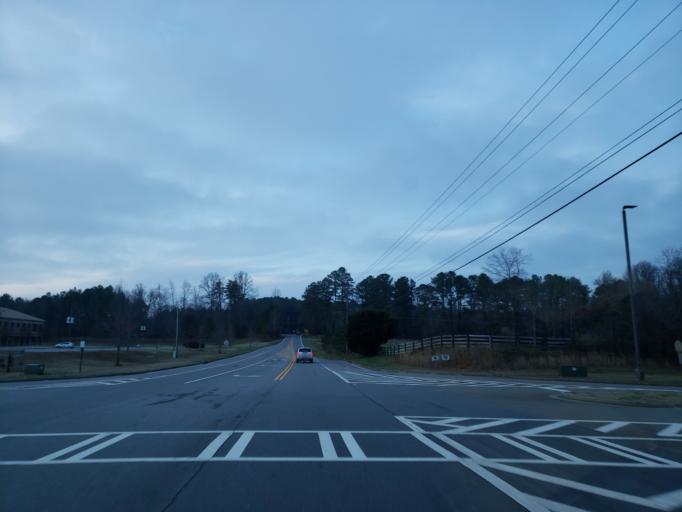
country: US
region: Georgia
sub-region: Fulton County
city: Milton
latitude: 34.2360
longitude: -84.3349
